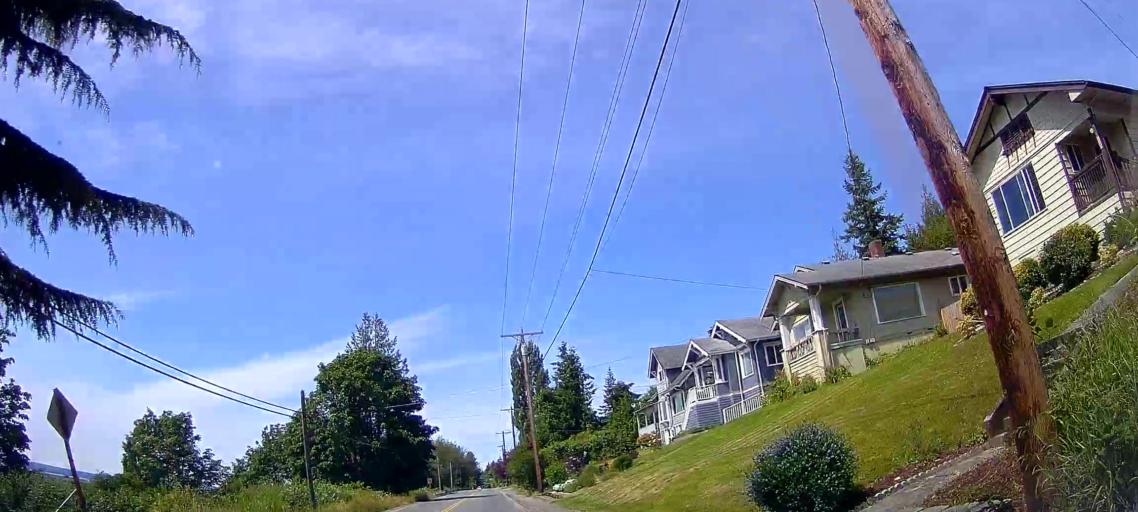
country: US
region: Washington
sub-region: Snohomish County
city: Stanwood
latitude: 48.2455
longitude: -122.3484
